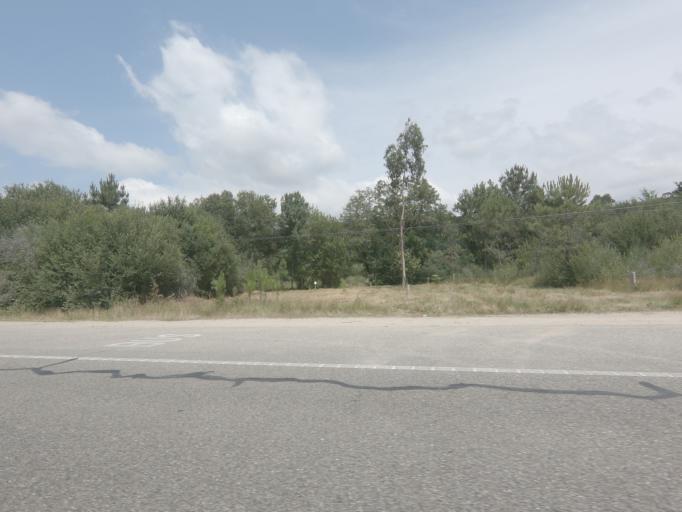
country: ES
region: Galicia
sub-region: Provincia de Pontevedra
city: Tomino
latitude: 42.0209
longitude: -8.7326
